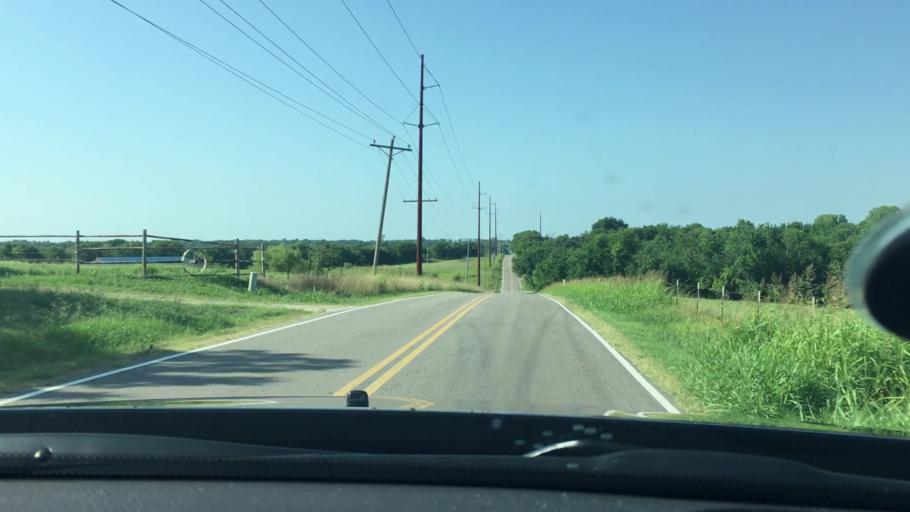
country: US
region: Oklahoma
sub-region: Pontotoc County
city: Ada
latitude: 34.8010
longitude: -96.6348
